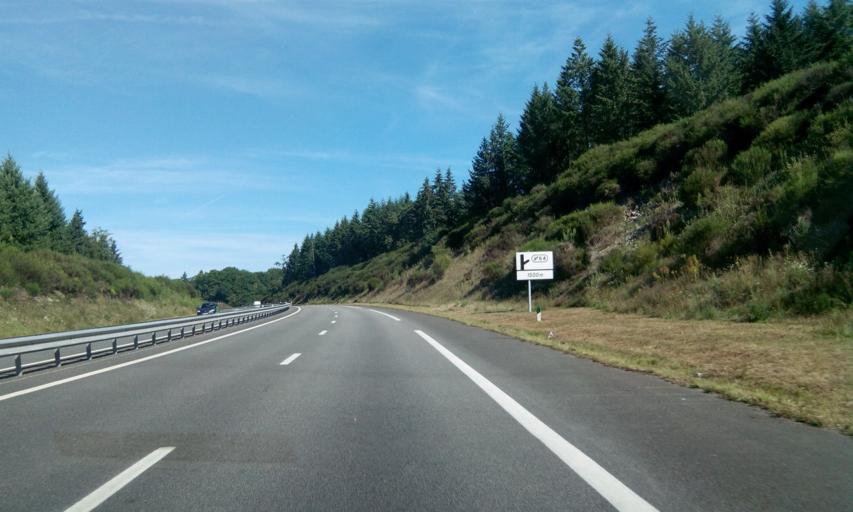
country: FR
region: Limousin
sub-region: Departement de la Haute-Vienne
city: Verneuil-sur-Vienne
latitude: 45.8710
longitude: 1.1180
